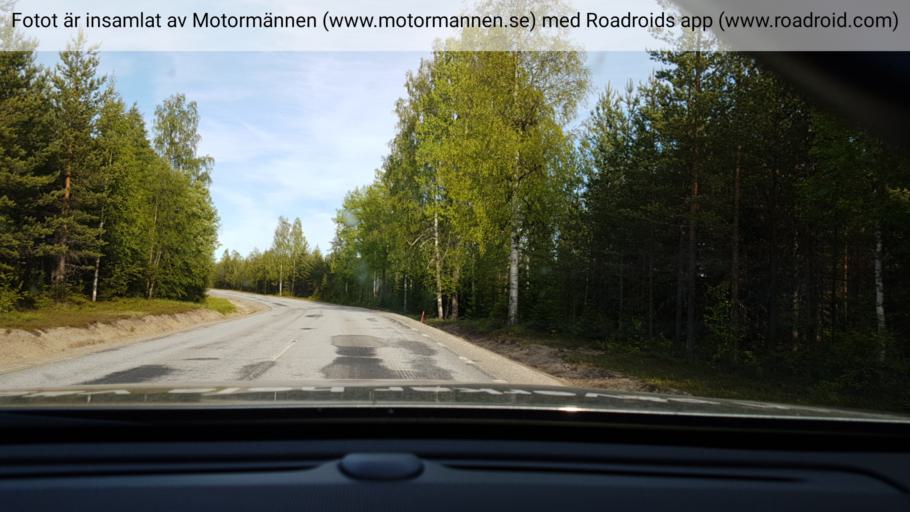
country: SE
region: Vaesterbotten
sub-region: Vindelns Kommun
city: Vindeln
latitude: 64.1699
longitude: 19.7557
